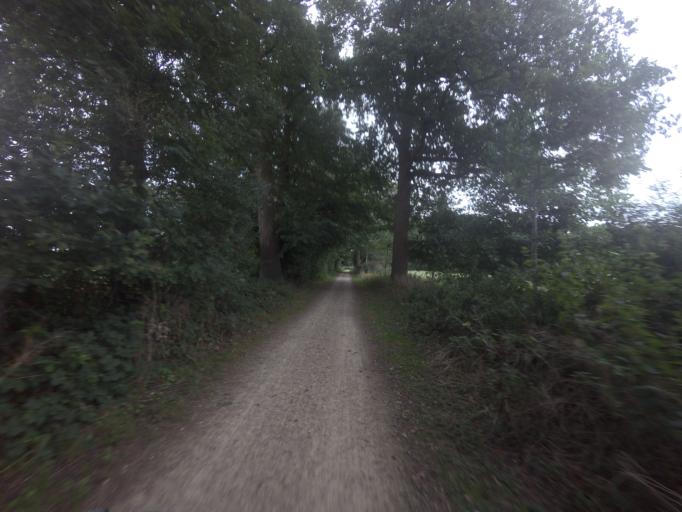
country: NL
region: Overijssel
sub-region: Gemeente Raalte
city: Raalte
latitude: 52.3238
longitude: 6.2879
